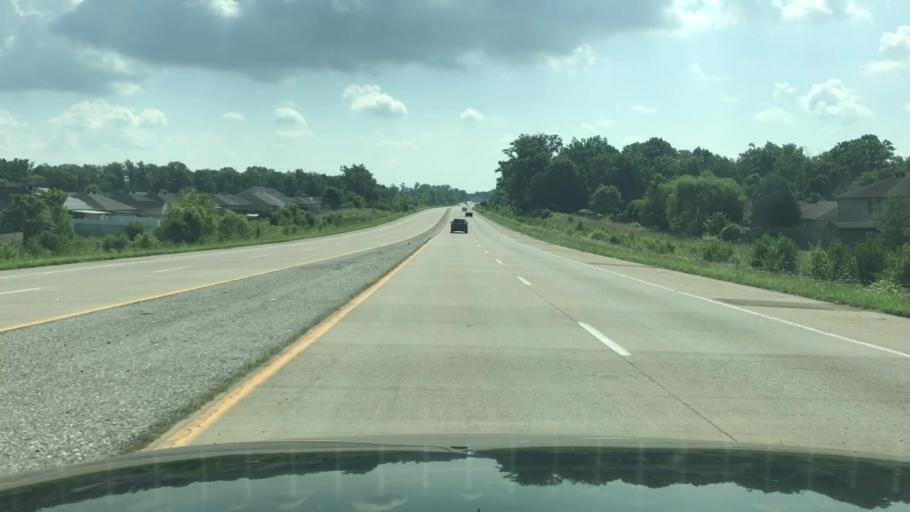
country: US
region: Indiana
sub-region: Vanderburgh County
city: Melody Hill
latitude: 38.0131
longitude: -87.5071
